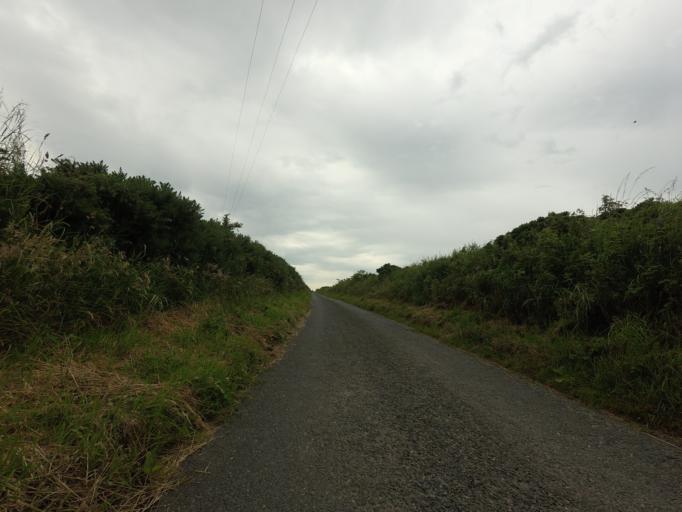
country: GB
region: Scotland
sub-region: Aberdeenshire
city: Whitehills
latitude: 57.6726
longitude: -2.5985
